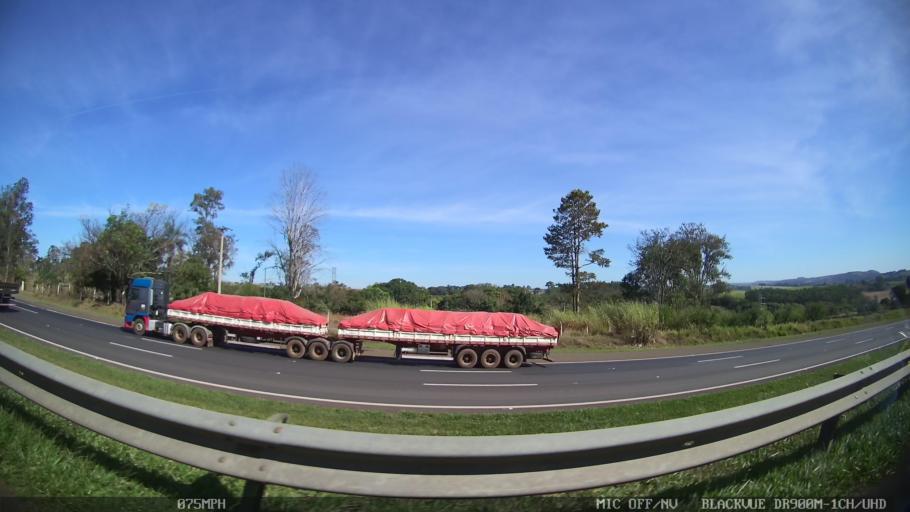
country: BR
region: Sao Paulo
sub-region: Pirassununga
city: Pirassununga
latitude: -22.0653
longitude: -47.4258
